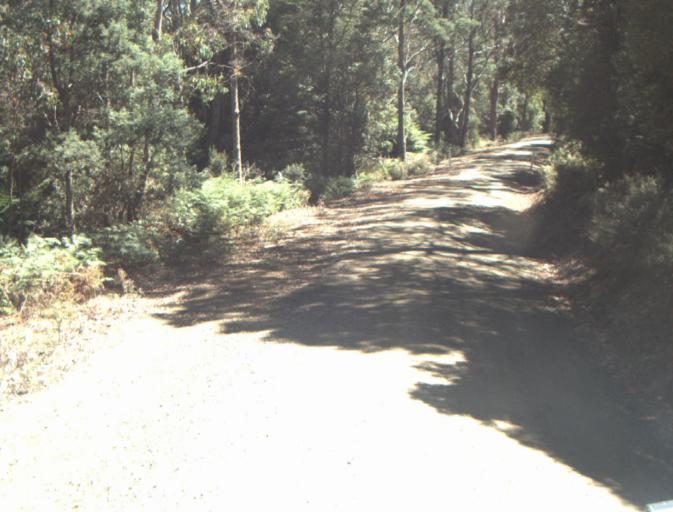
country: AU
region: Tasmania
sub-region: Dorset
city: Scottsdale
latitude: -41.3582
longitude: 147.4267
